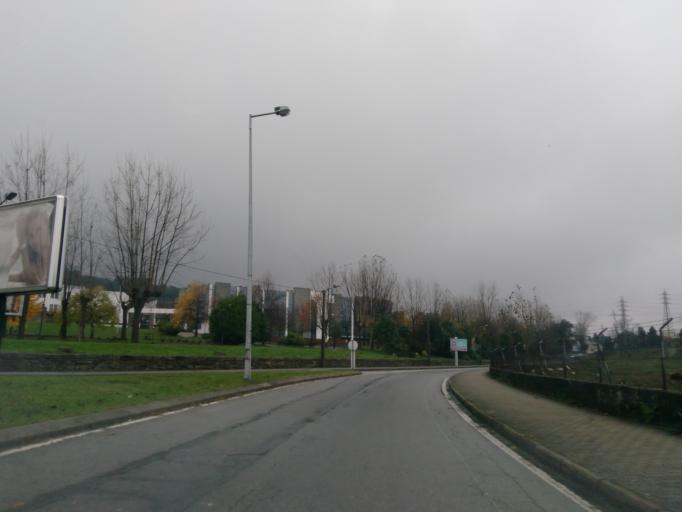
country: PT
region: Braga
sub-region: Braga
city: Braga
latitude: 41.5583
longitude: -8.3975
